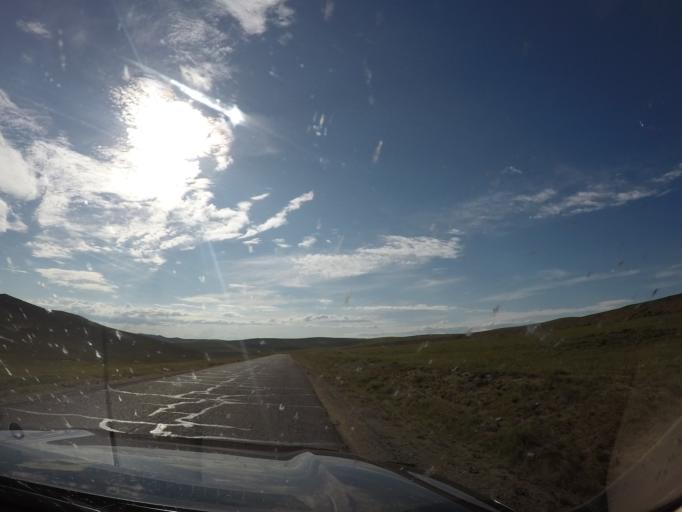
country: MN
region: Hentiy
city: Modot
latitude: 47.8054
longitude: 108.7206
